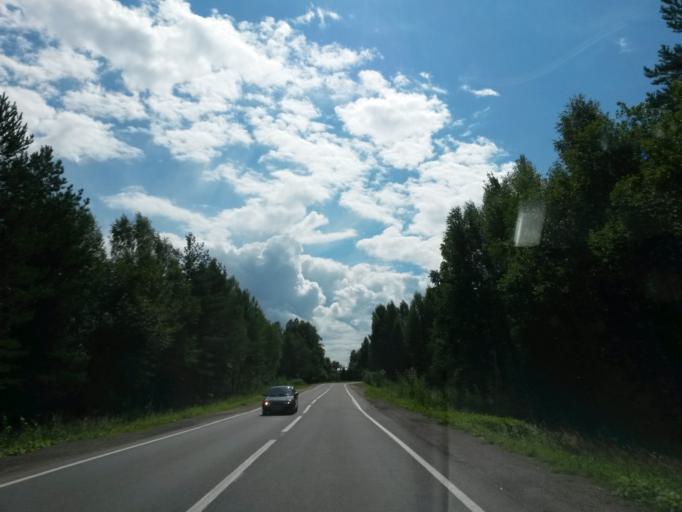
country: RU
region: Jaroslavl
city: Gavrilov-Yam
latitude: 57.2844
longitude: 39.9533
